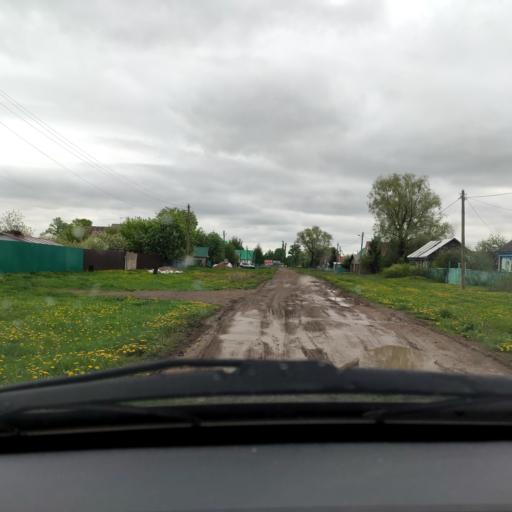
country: RU
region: Bashkortostan
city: Asanovo
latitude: 55.0016
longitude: 55.4877
